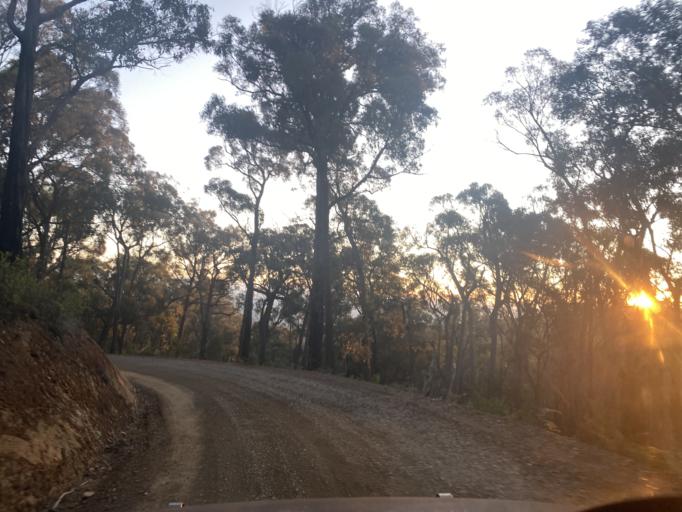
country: AU
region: Victoria
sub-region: Yarra Ranges
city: Healesville
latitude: -37.4258
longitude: 145.5143
